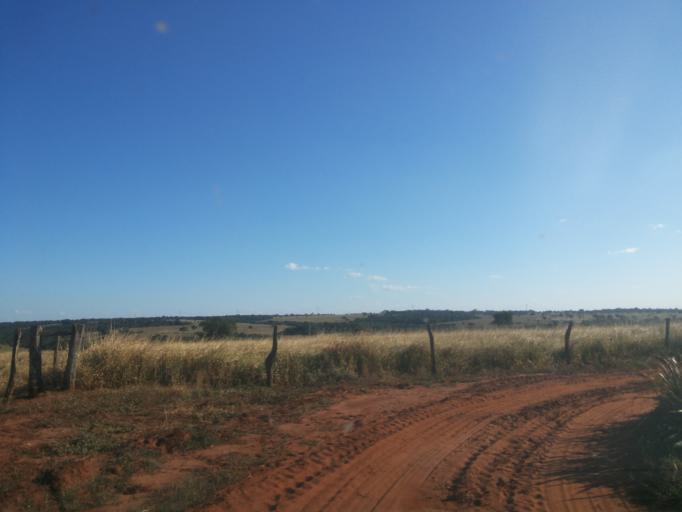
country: BR
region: Minas Gerais
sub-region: Centralina
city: Centralina
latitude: -18.7548
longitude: -49.0998
